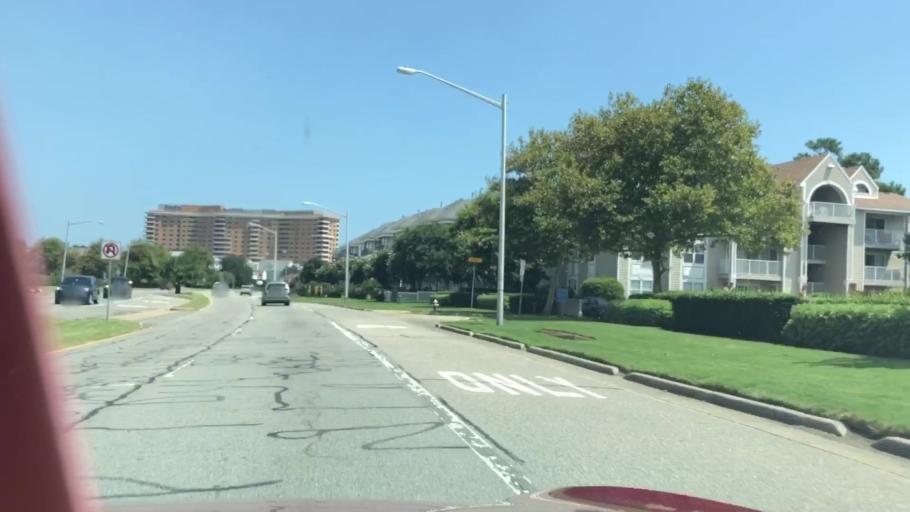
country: US
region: Virginia
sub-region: City of Virginia Beach
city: Virginia Beach
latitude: 36.9080
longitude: -76.0846
